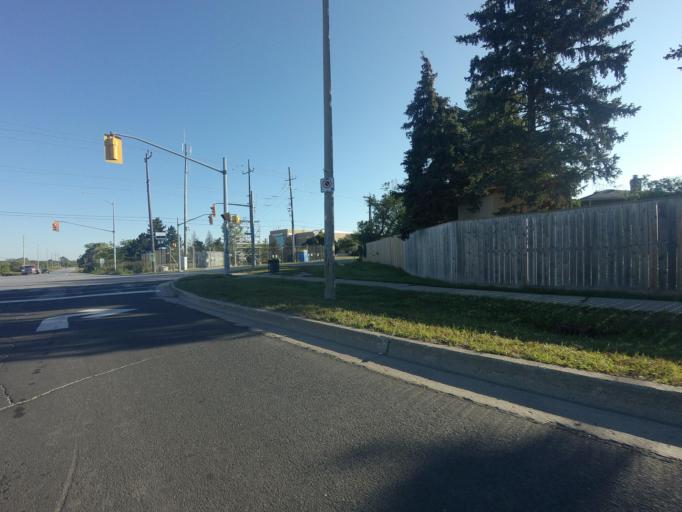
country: CA
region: Ontario
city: Bradford West Gwillimbury
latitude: 44.0341
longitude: -79.8096
